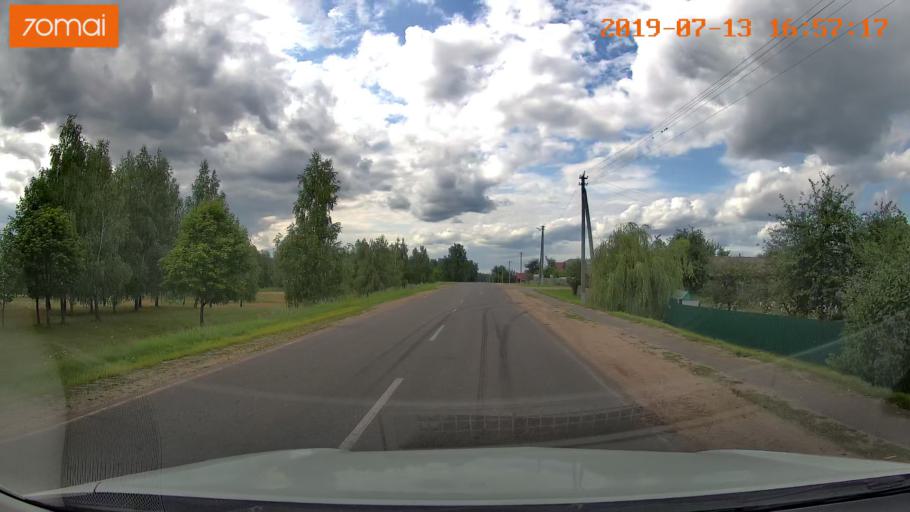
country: BY
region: Mogilev
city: Kirawsk
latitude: 53.2786
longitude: 29.4531
